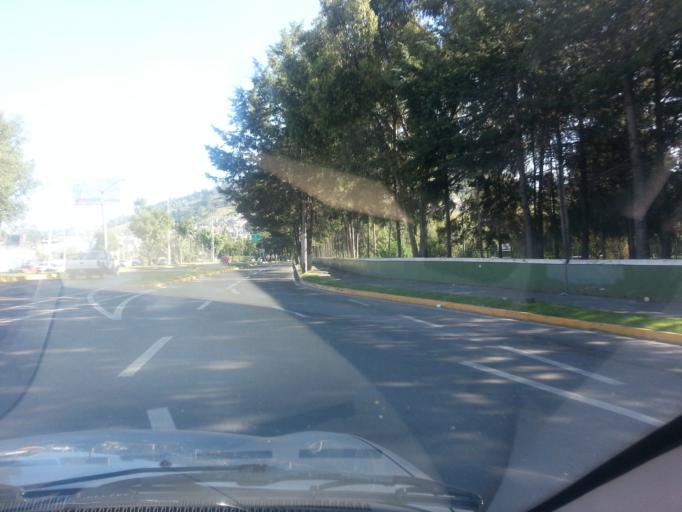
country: MX
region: Mexico
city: San Buenaventura
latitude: 19.2850
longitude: -99.6804
